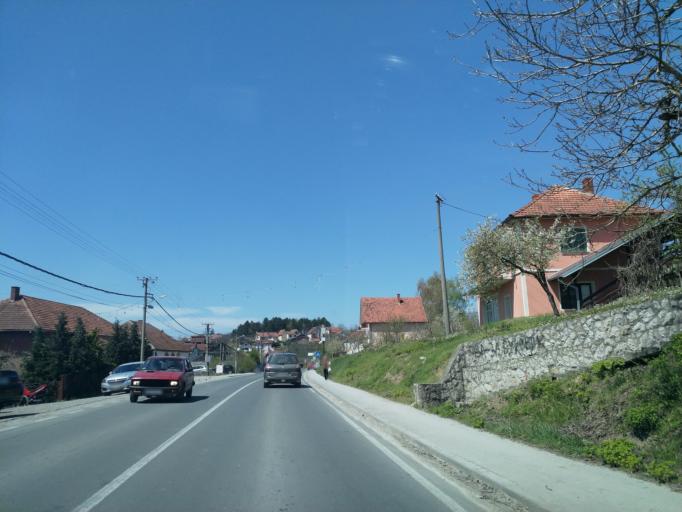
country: RS
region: Central Serbia
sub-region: Sumadijski Okrug
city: Arangelovac
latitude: 44.3277
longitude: 20.5220
